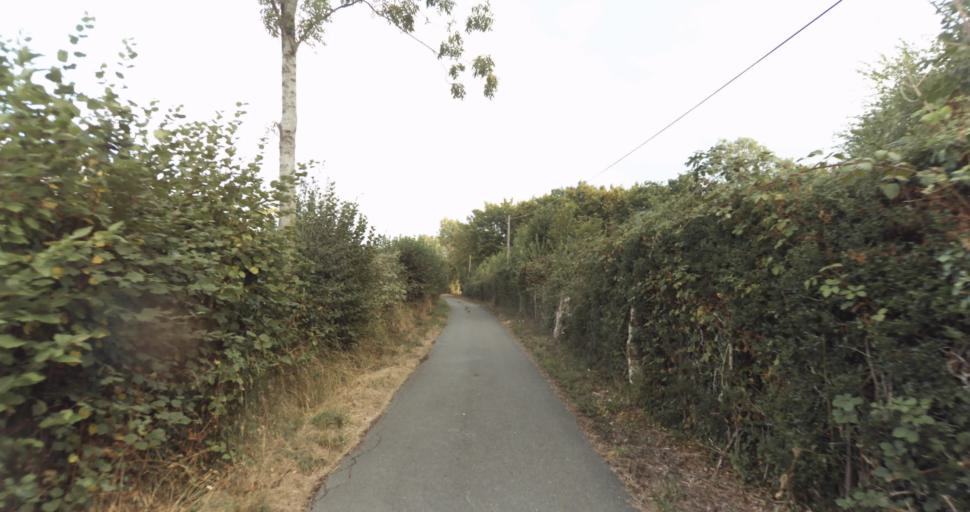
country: FR
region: Lower Normandy
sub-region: Departement de l'Orne
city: Vimoutiers
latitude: 48.9416
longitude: 0.2177
